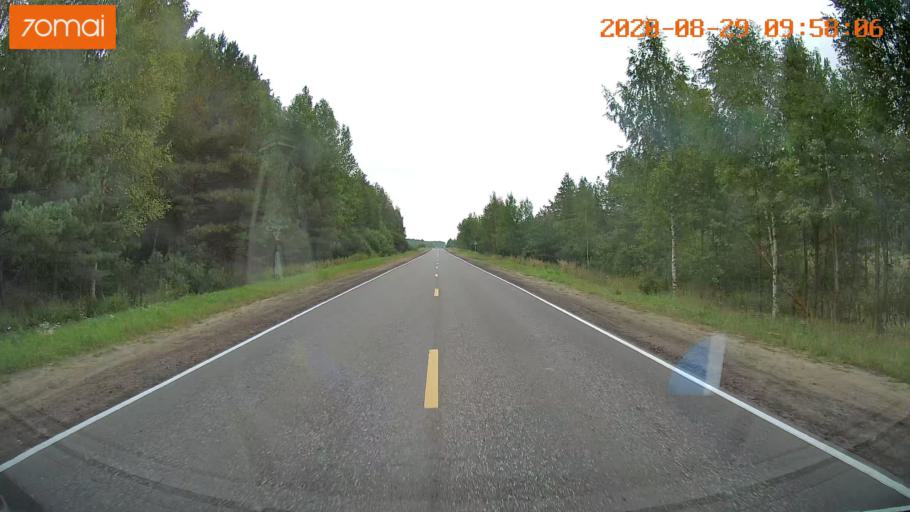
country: RU
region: Ivanovo
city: Zarechnyy
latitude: 57.4144
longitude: 42.3308
